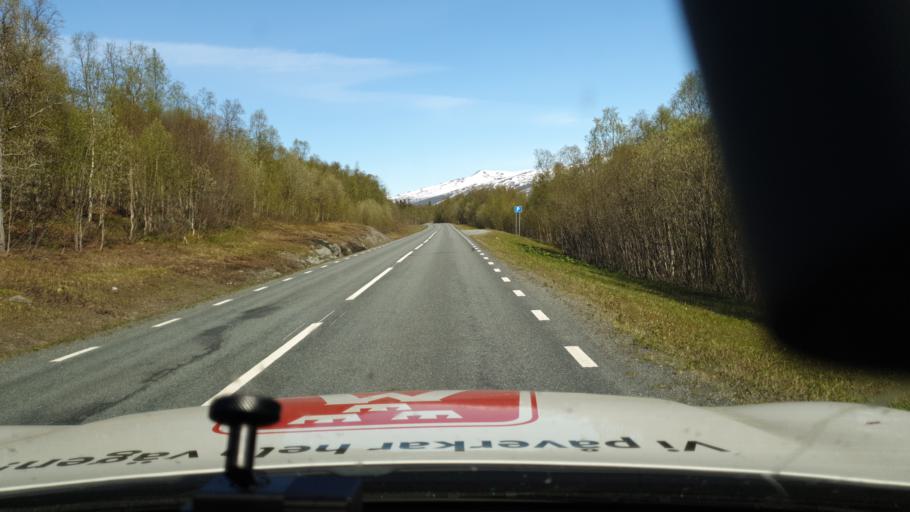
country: NO
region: Nordland
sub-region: Rana
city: Mo i Rana
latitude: 65.7648
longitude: 15.1148
